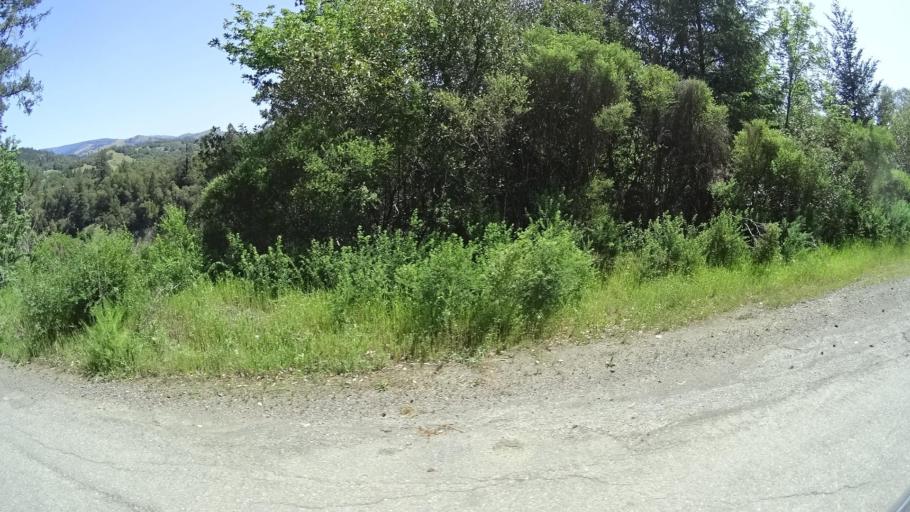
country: US
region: California
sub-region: Humboldt County
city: Redway
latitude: 40.1709
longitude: -123.6046
